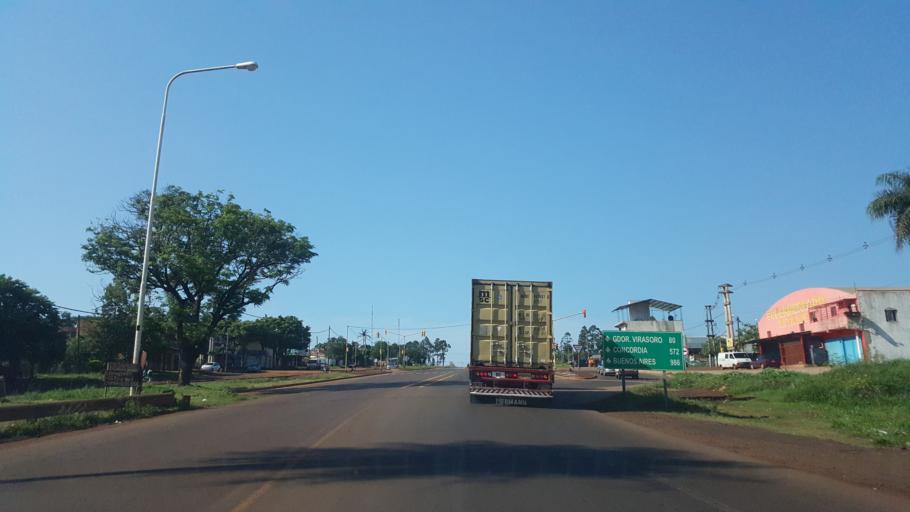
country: AR
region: Misiones
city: Garupa
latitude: -27.4656
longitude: -55.8631
